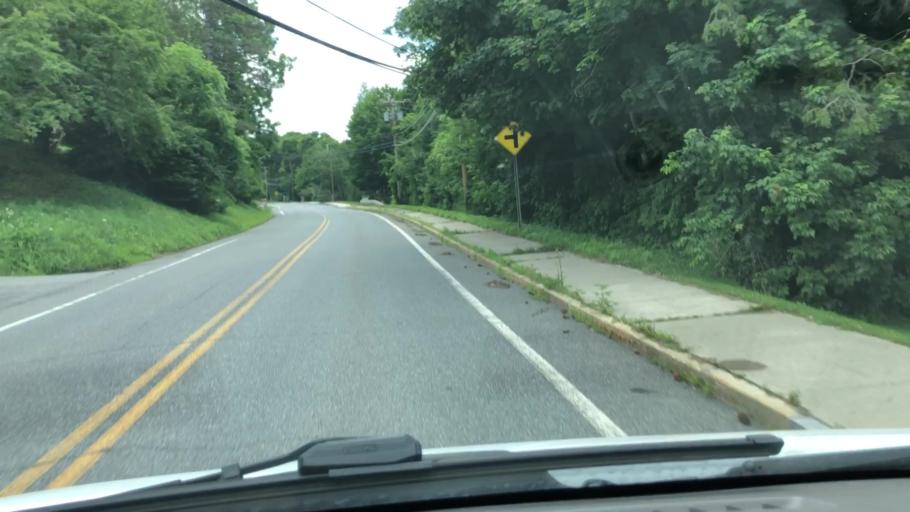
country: US
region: Massachusetts
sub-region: Berkshire County
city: Adams
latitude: 42.6143
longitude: -73.1180
